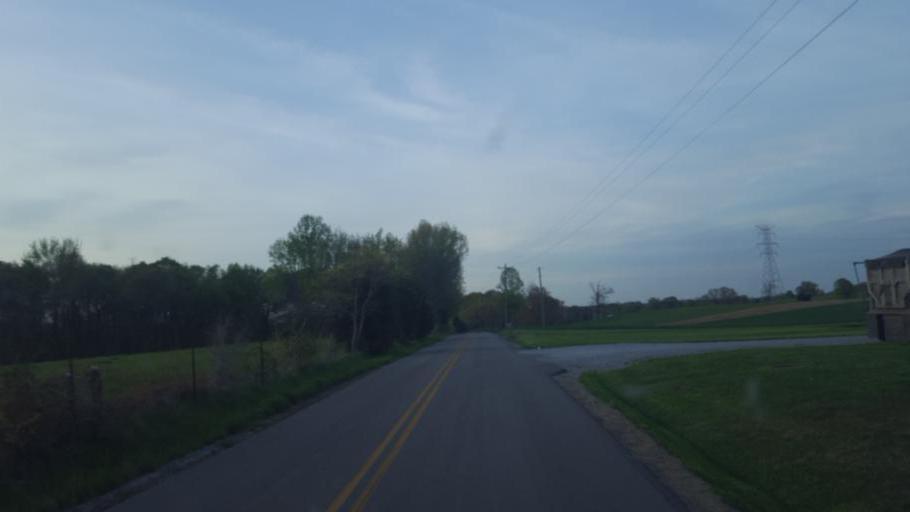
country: US
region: Kentucky
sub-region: Metcalfe County
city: Edmonton
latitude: 37.0442
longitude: -85.7076
